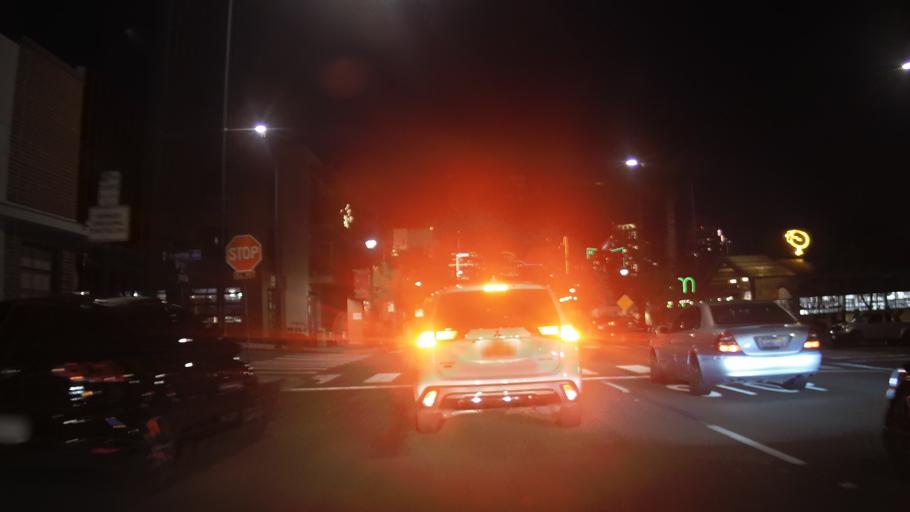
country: US
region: California
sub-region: San Diego County
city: San Diego
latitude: 32.7284
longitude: -117.1713
